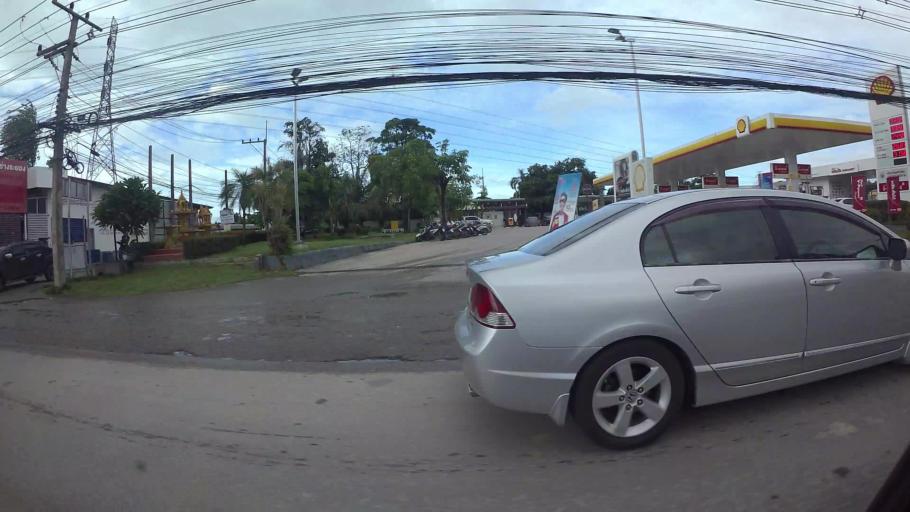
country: TH
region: Rayong
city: Rayong
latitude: 12.6950
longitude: 101.1990
